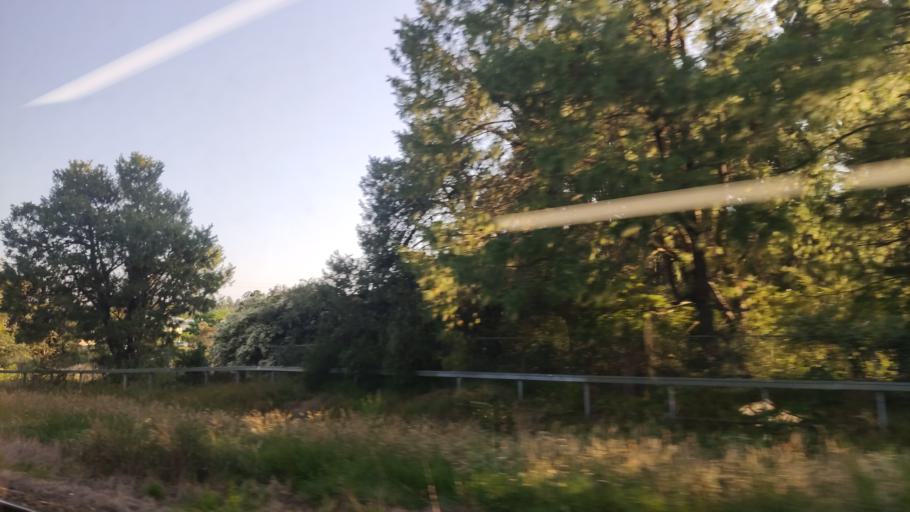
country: AU
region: New South Wales
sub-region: Blue Mountains Municipality
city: Leura
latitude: -33.7067
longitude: 150.3743
